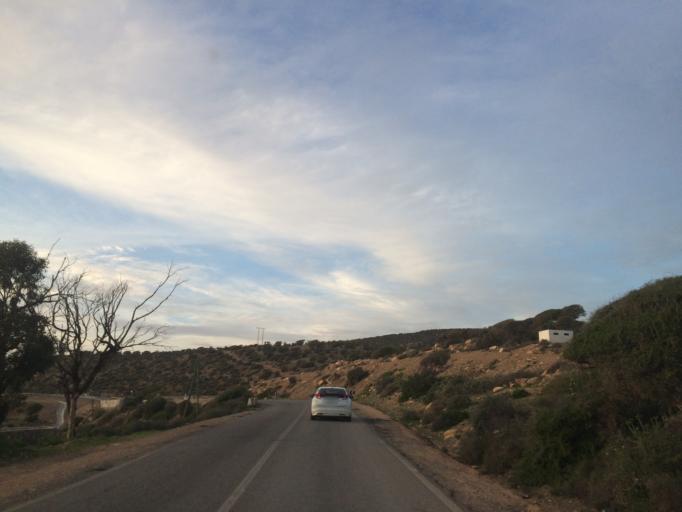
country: MA
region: Souss-Massa-Draa
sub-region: Agadir-Ida-ou-Tnan
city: Taghazout
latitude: 30.5476
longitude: -9.7264
